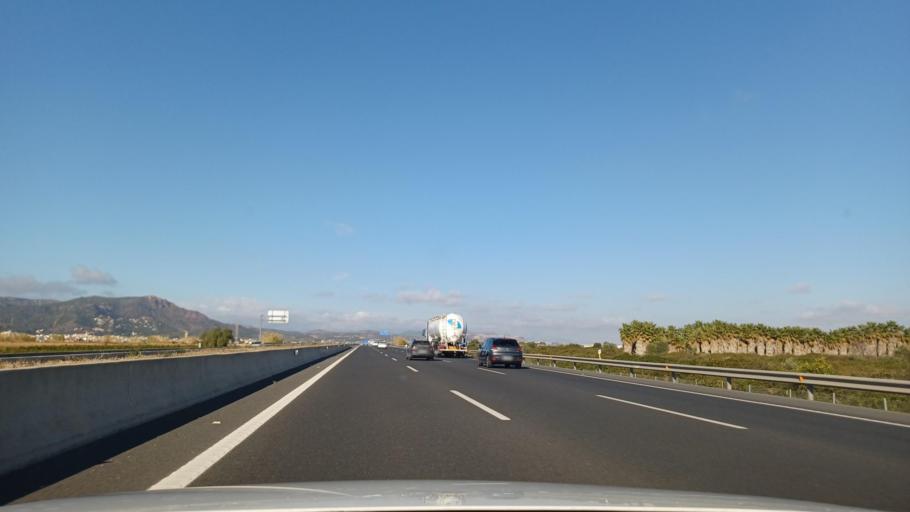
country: ES
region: Valencia
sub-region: Provincia de Valencia
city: Puig
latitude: 39.5973
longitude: -0.2928
